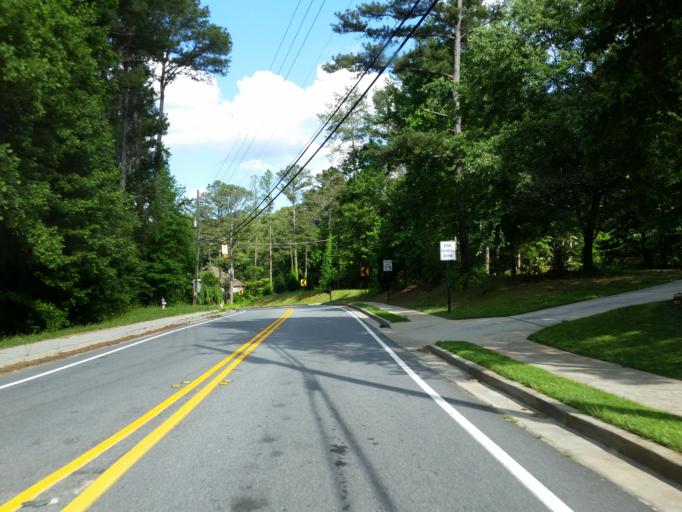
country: US
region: Georgia
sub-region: Fulton County
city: Roswell
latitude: 34.0158
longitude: -84.4196
